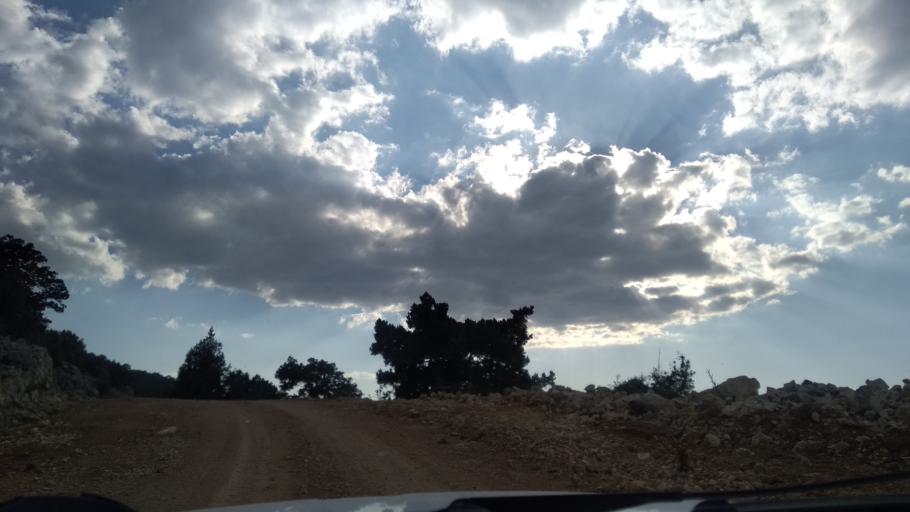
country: TR
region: Mersin
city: Sarikavak
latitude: 36.5998
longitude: 33.7023
